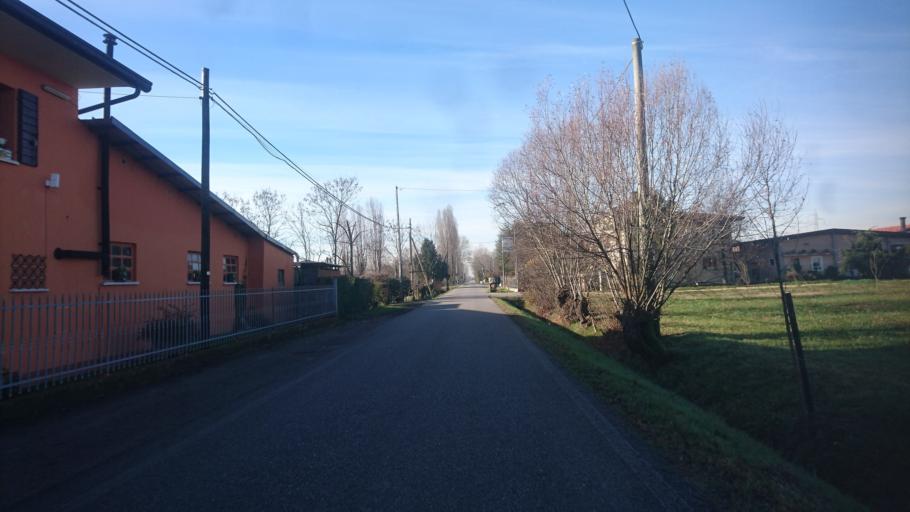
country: IT
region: Veneto
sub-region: Provincia di Padova
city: Tremignon
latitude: 45.5162
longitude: 11.7848
